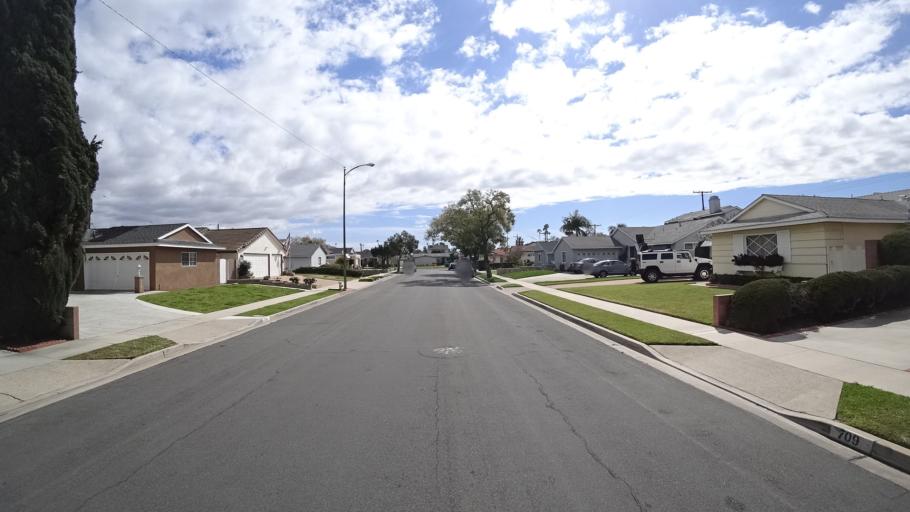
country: US
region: California
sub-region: Orange County
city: Anaheim
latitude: 33.8226
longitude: -117.9477
